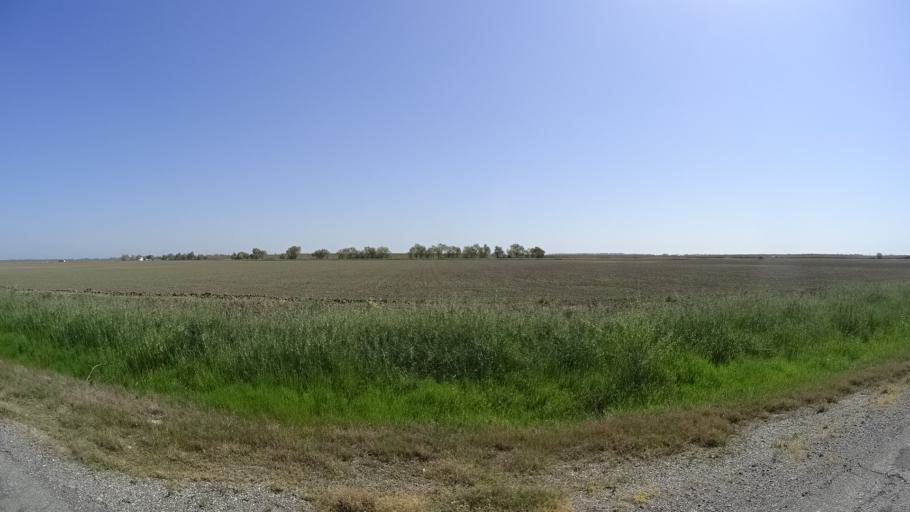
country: US
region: California
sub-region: Glenn County
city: Willows
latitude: 39.5153
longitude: -122.0373
